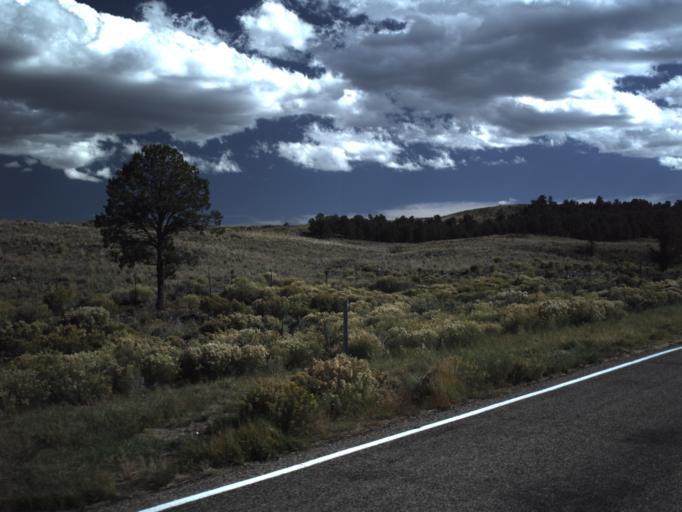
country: US
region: Utah
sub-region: Garfield County
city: Panguitch
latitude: 37.7857
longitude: -112.4396
